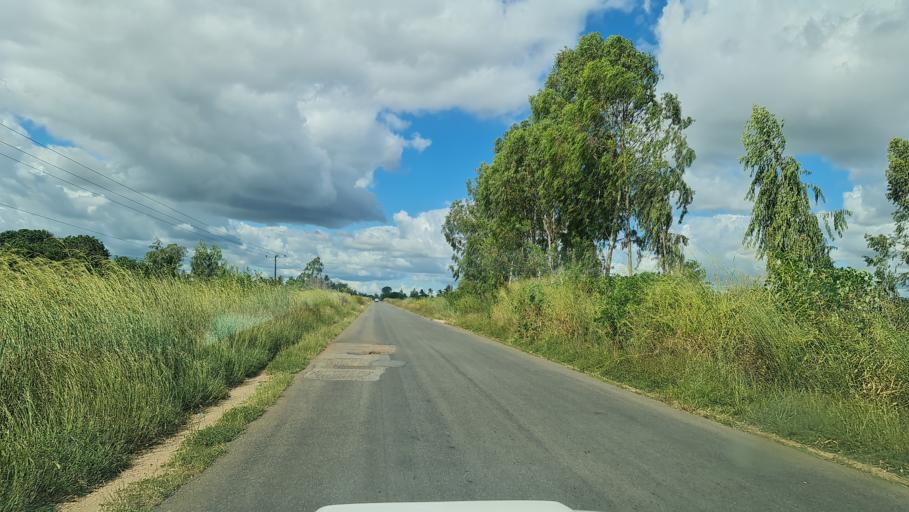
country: MZ
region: Zambezia
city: Quelimane
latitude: -17.5906
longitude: 36.7649
